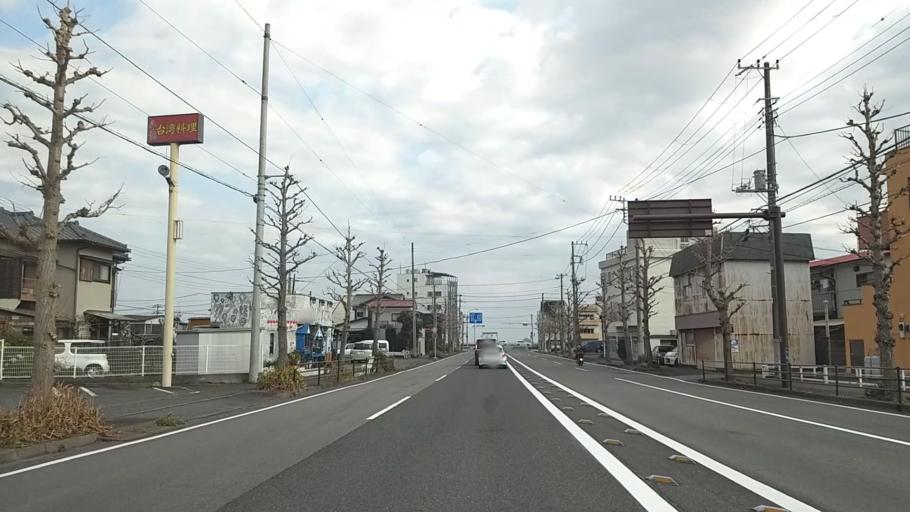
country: JP
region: Shizuoka
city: Ito
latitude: 35.0082
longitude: 139.0830
